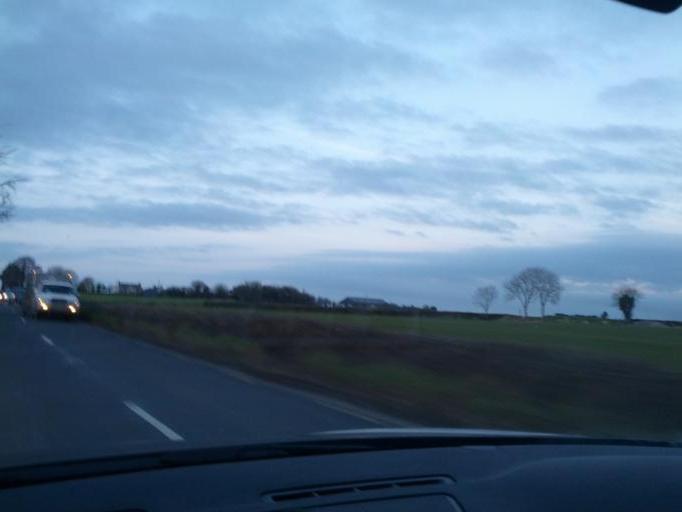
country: IE
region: Connaught
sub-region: County Galway
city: Portumna
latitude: 53.0447
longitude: -8.1106
